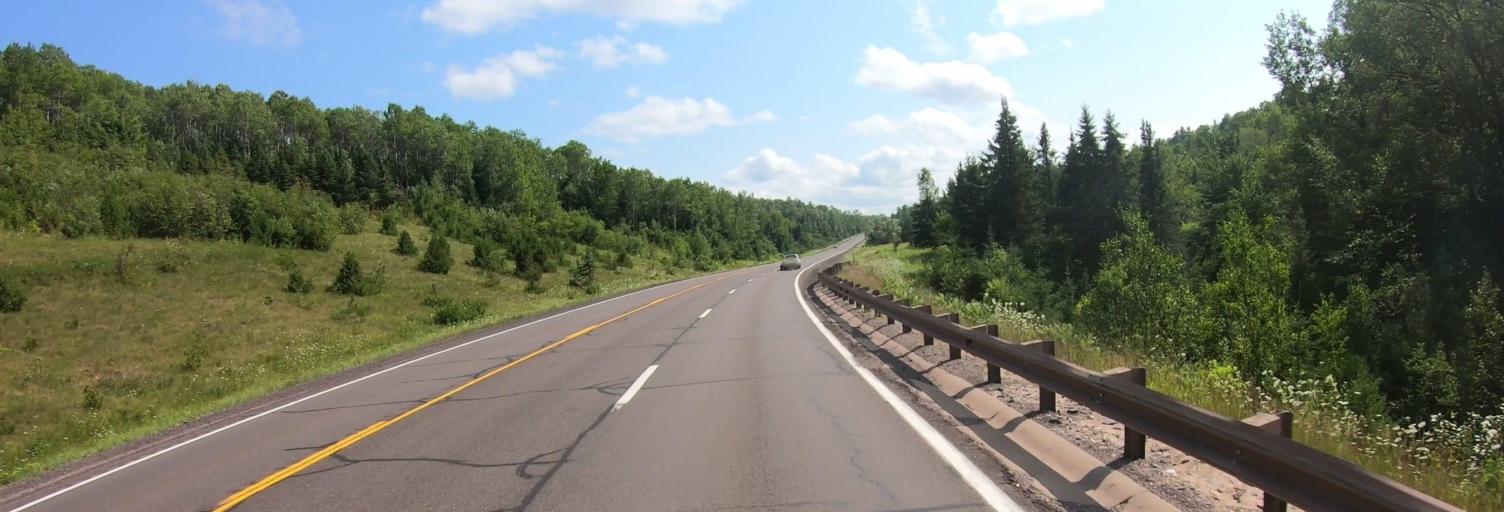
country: US
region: Michigan
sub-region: Ontonagon County
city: Ontonagon
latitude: 46.6876
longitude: -89.1649
